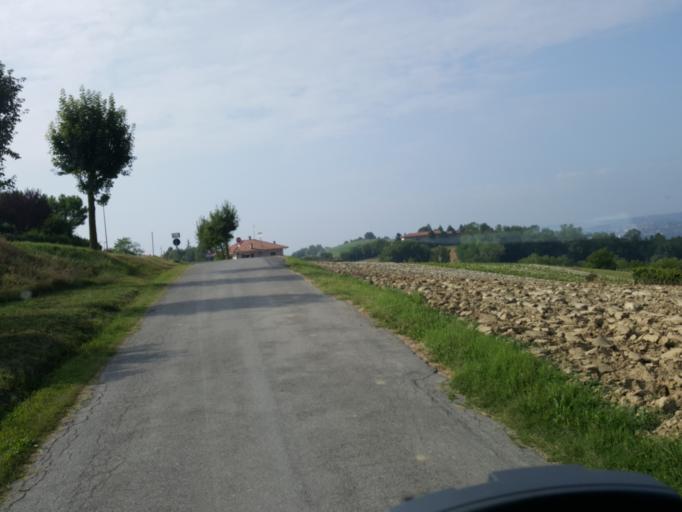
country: IT
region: Piedmont
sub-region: Provincia di Cuneo
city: Novello
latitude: 44.5898
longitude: 7.9240
